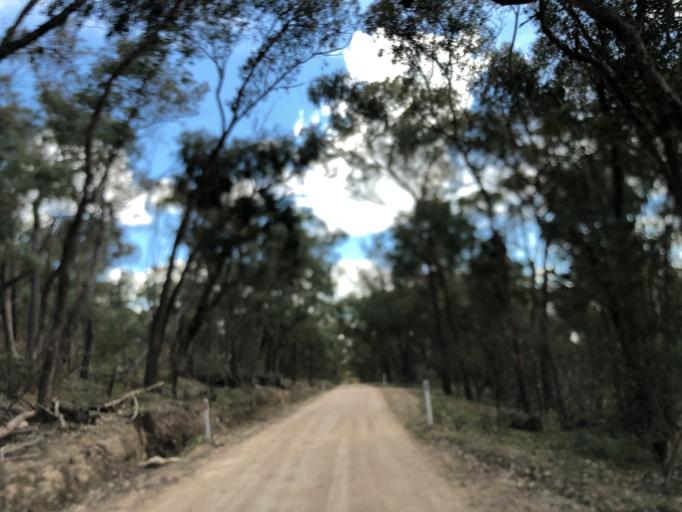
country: AU
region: Victoria
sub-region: Benalla
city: Benalla
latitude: -36.7397
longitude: 146.1545
